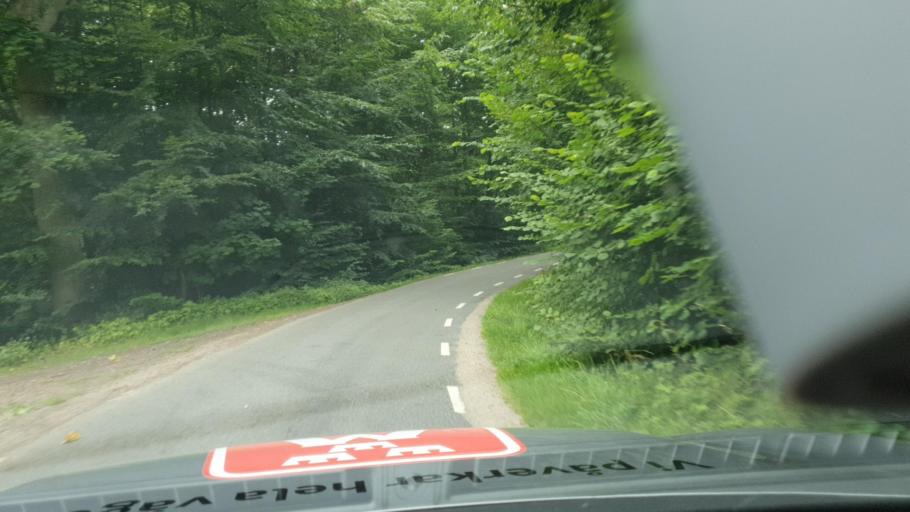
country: SE
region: Blekinge
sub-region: Solvesborgs Kommun
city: Soelvesborg
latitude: 56.0927
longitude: 14.5416
